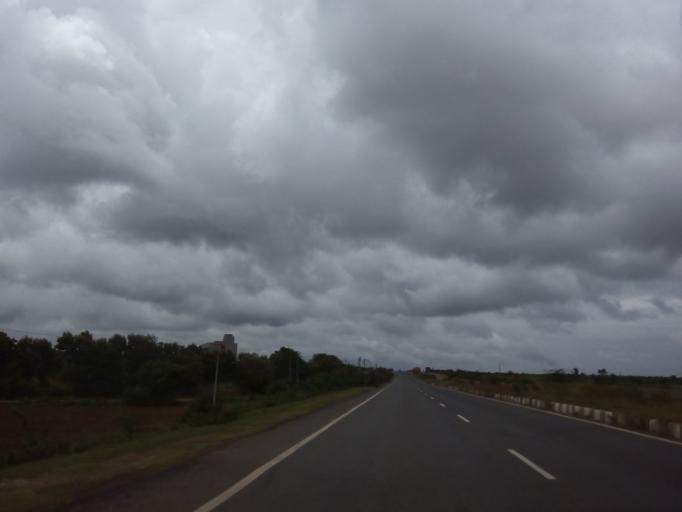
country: IN
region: Karnataka
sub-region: Haveri
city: Ranibennur
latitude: 14.6558
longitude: 75.5675
